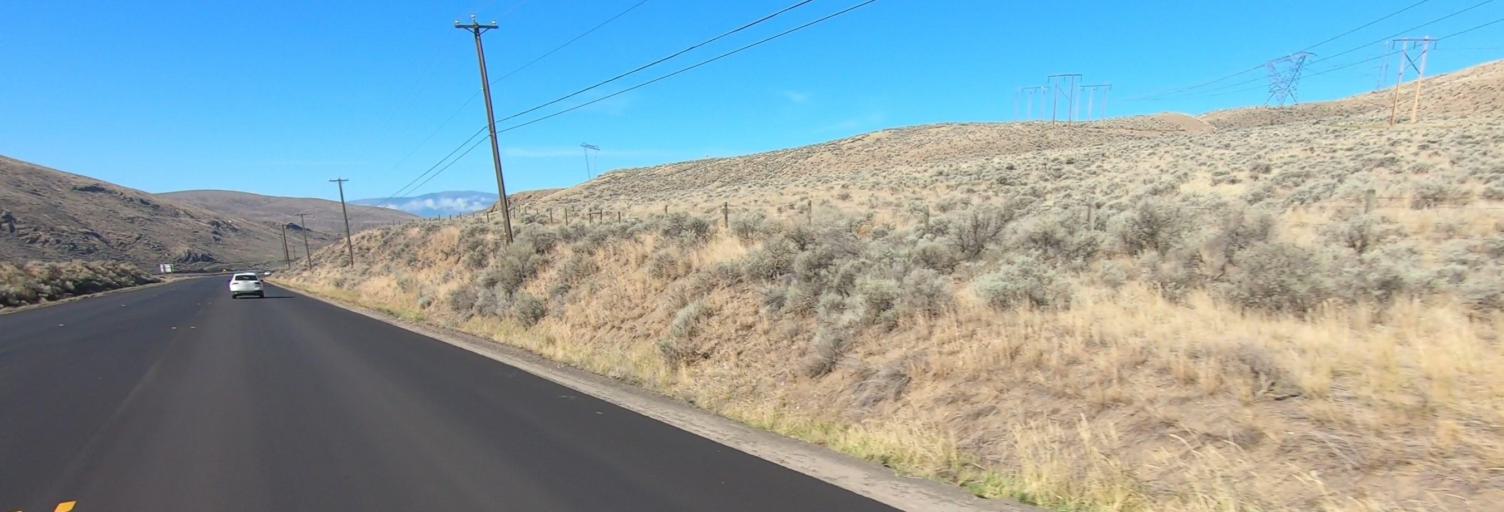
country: CA
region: British Columbia
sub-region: Thompson-Nicola Regional District
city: Ashcroft
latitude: 50.7889
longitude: -121.1787
